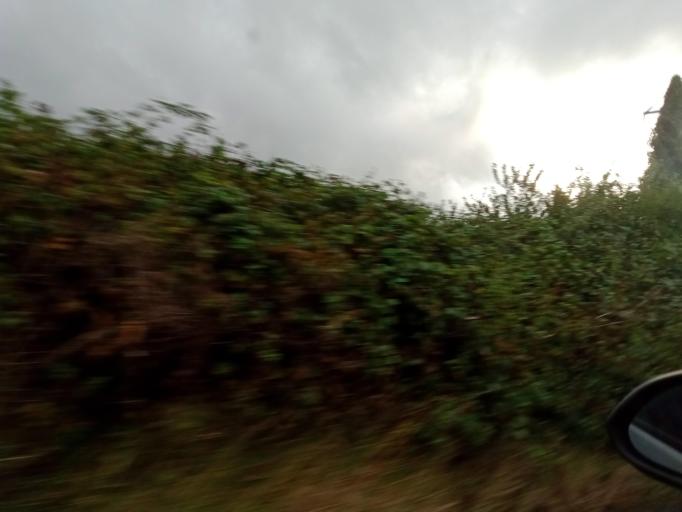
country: IE
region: Leinster
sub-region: Laois
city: Mountmellick
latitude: 53.1303
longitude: -7.3919
